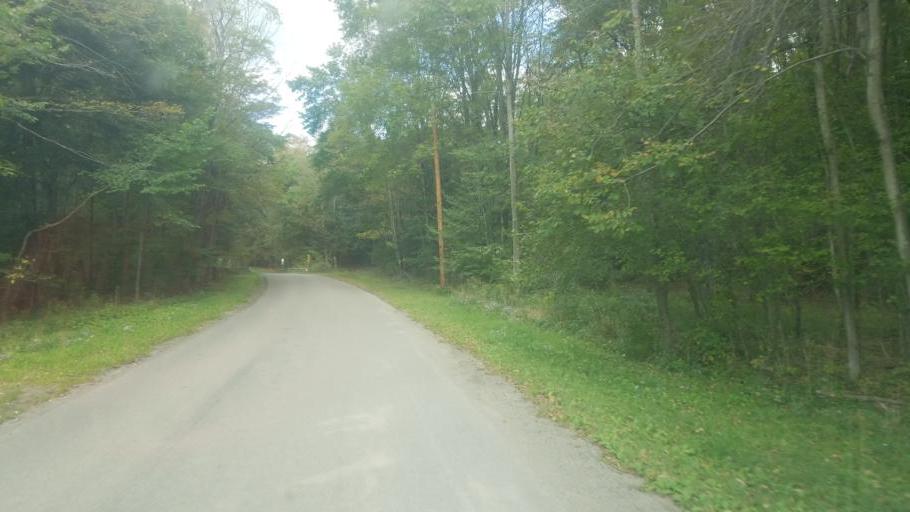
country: US
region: New York
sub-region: Cattaraugus County
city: Weston Mills
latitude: 42.1478
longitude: -78.3536
